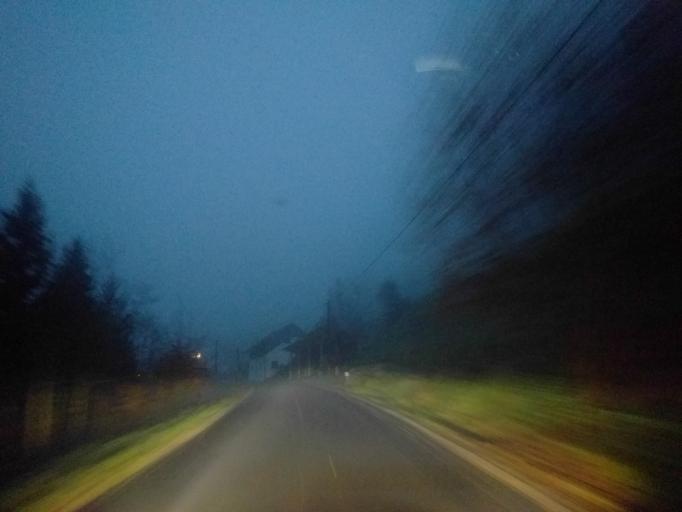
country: AT
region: Upper Austria
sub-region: Politischer Bezirk Urfahr-Umgebung
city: Kirchschlag bei Linz
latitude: 48.3955
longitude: 14.2968
